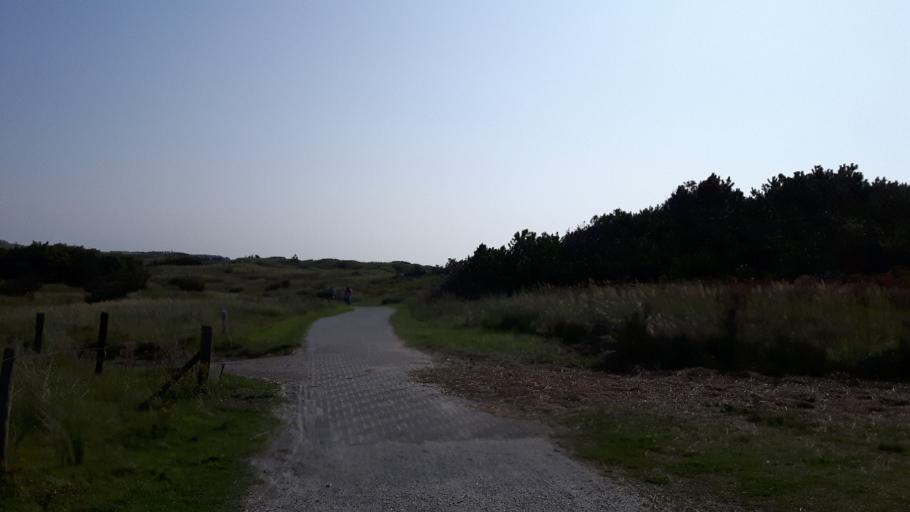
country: NL
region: Friesland
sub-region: Gemeente Ameland
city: Nes
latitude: 53.4591
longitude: 5.7829
